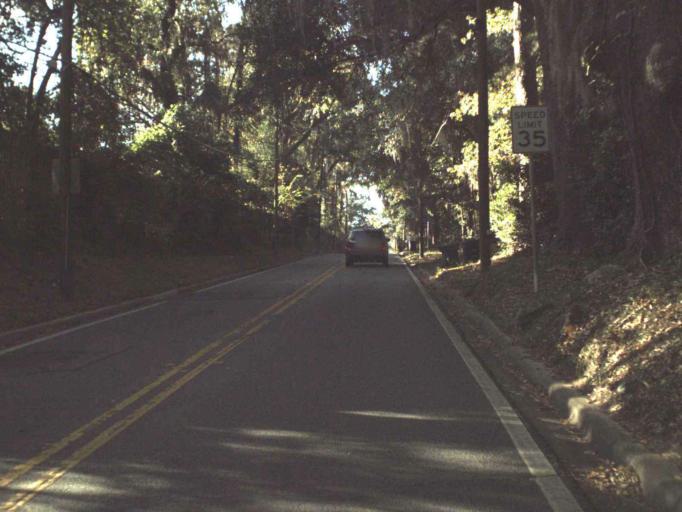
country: US
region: Florida
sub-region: Leon County
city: Tallahassee
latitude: 30.4604
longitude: -84.2772
